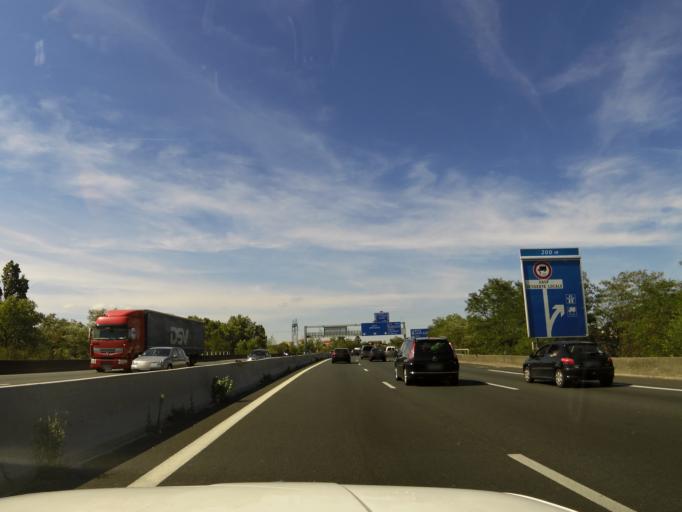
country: FR
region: Rhone-Alpes
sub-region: Departement de l'Isere
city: Chasse-sur-Rhone
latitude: 45.5759
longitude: 4.8055
